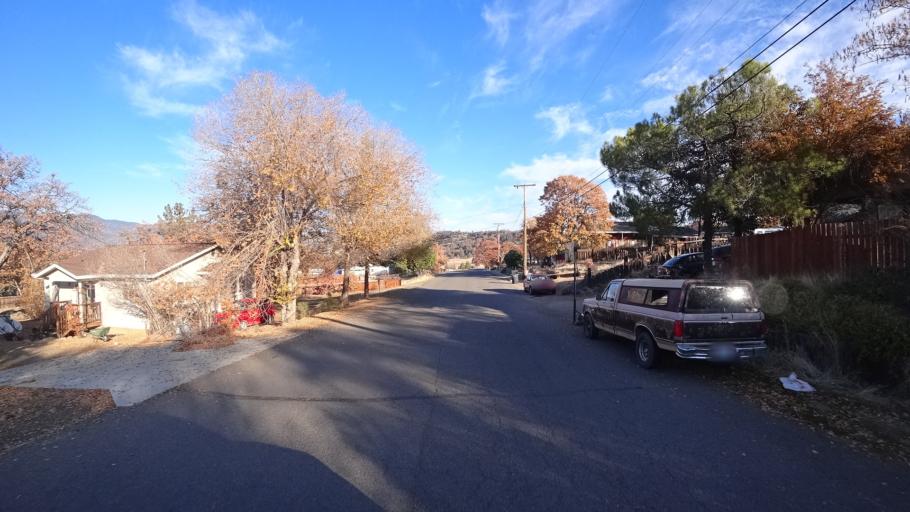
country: US
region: California
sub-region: Siskiyou County
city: Yreka
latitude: 41.7085
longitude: -122.6173
